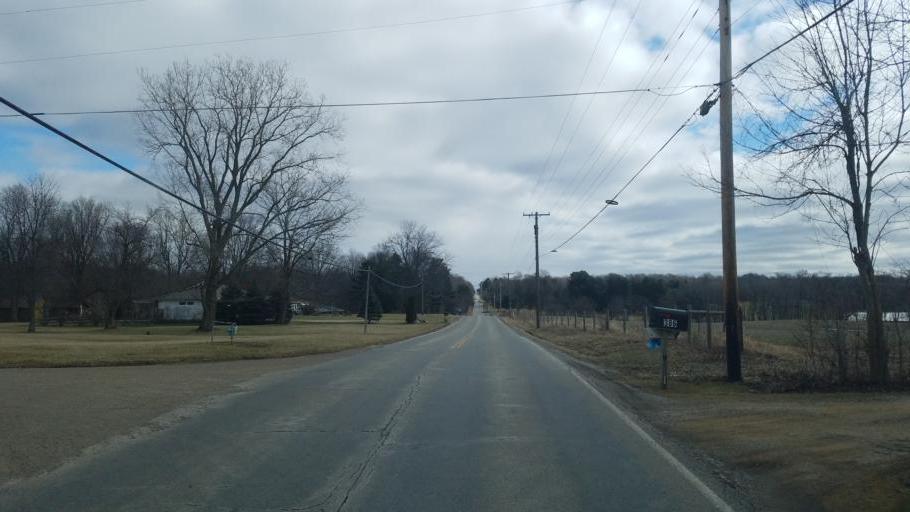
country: US
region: Ohio
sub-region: Richland County
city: Mansfield
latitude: 40.6959
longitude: -82.4971
